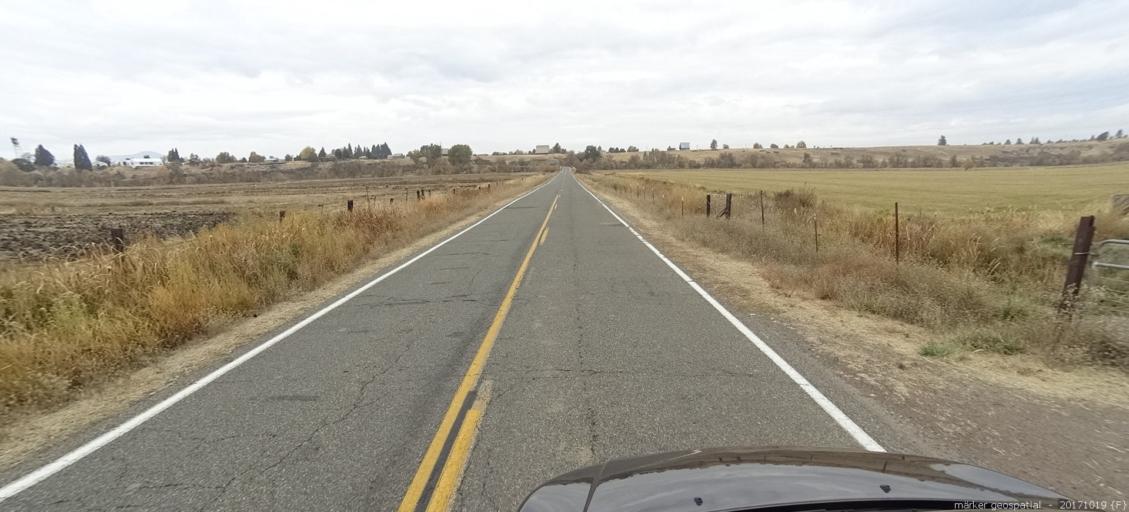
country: US
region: California
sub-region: Shasta County
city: Burney
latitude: 41.0447
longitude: -121.3888
